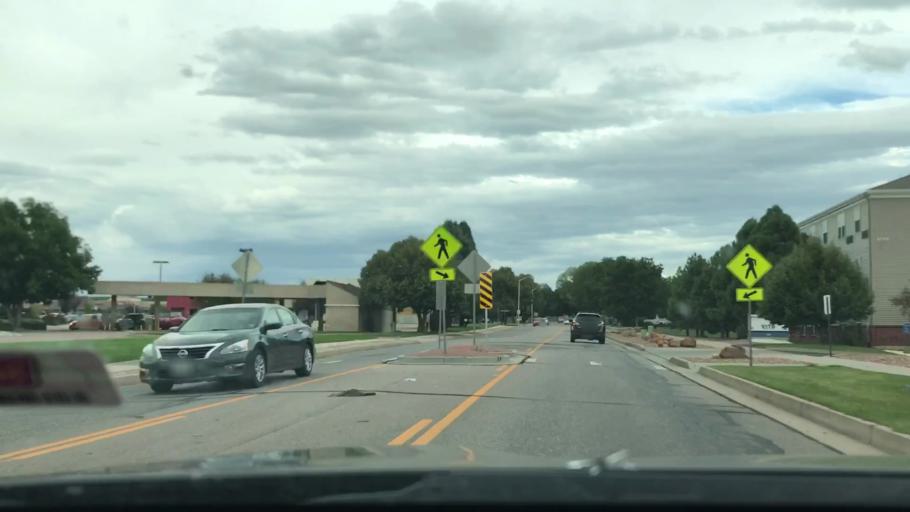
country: US
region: Colorado
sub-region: El Paso County
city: Cimarron Hills
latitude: 38.8896
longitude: -104.7634
